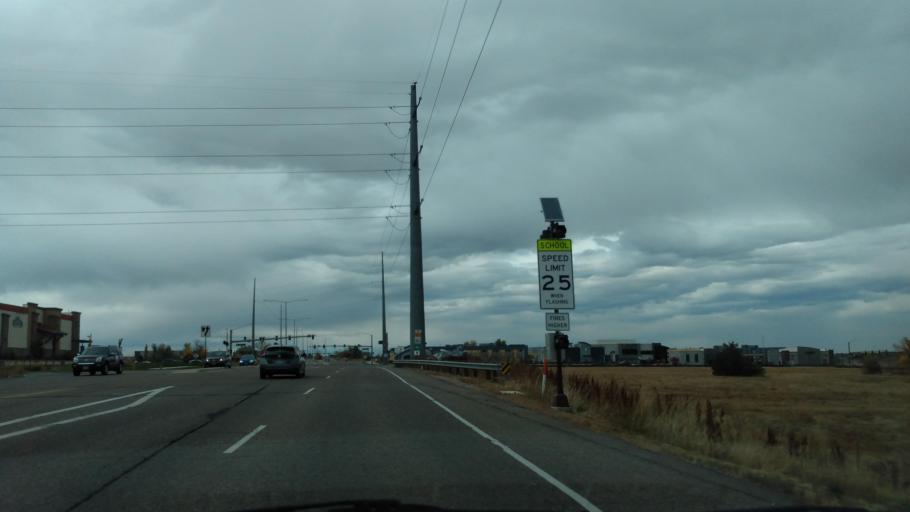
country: US
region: Colorado
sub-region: Adams County
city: Northglenn
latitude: 39.9555
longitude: -104.9782
